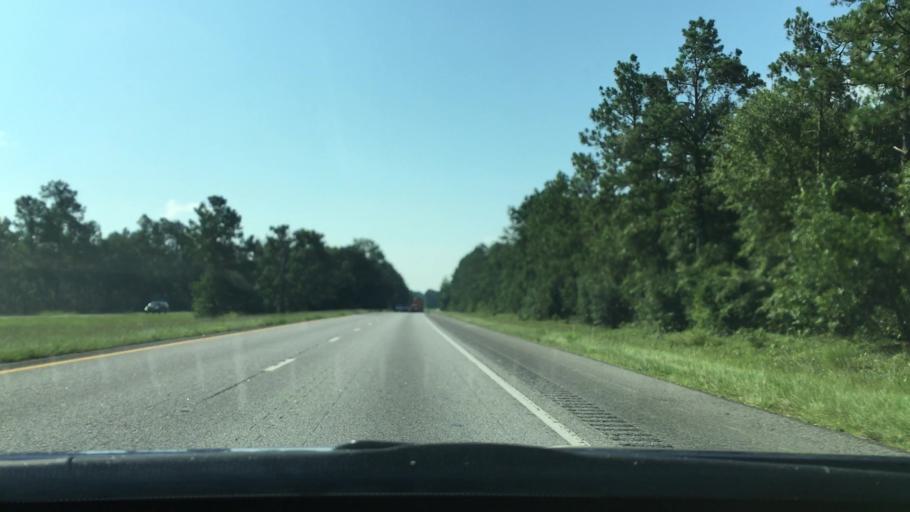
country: US
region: South Carolina
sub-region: Dorchester County
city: Ridgeville
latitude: 33.1721
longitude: -80.3672
